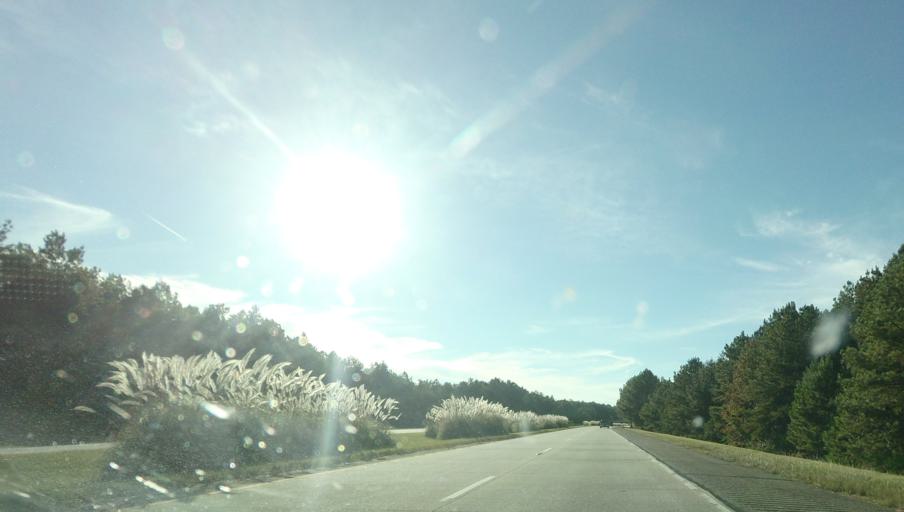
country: US
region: Georgia
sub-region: Muscogee County
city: Columbus
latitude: 32.5545
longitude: -84.9004
